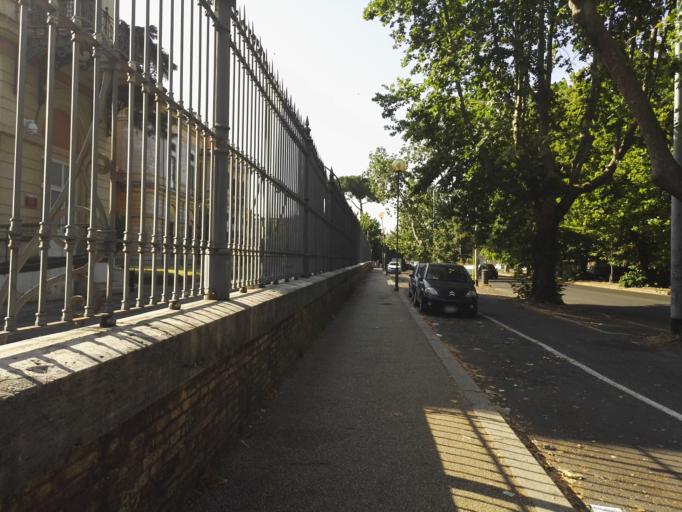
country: IT
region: Latium
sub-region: Citta metropolitana di Roma Capitale
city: Rome
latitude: 41.9050
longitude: 12.5105
